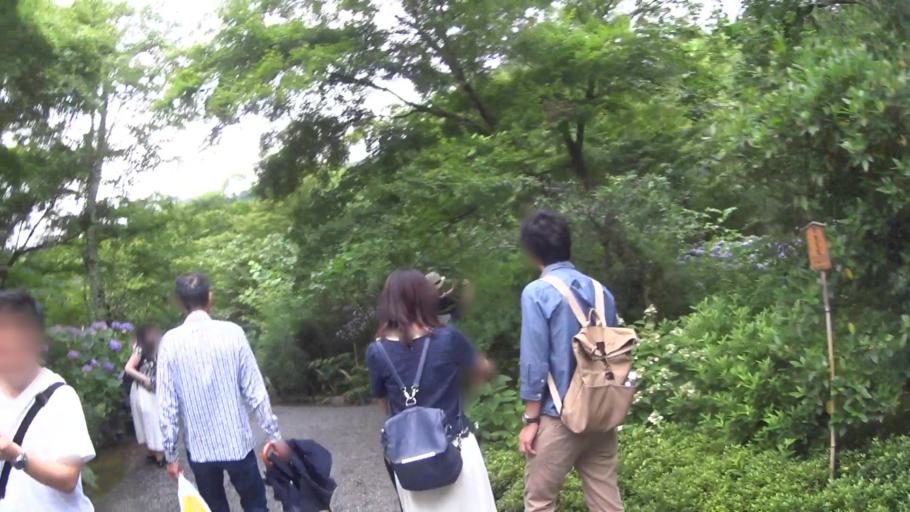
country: JP
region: Kyoto
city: Muko
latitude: 35.0169
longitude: 135.6728
